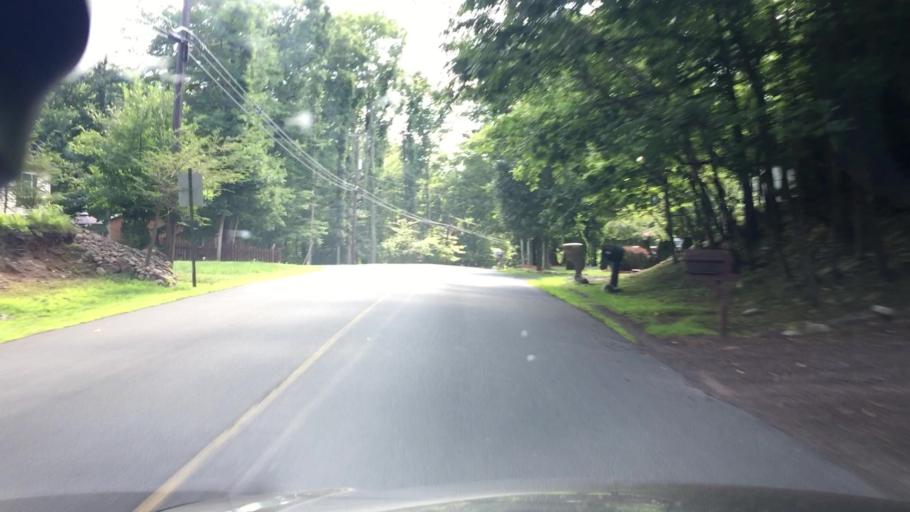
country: US
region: Pennsylvania
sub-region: Luzerne County
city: Freeland
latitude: 41.0430
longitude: -75.9318
